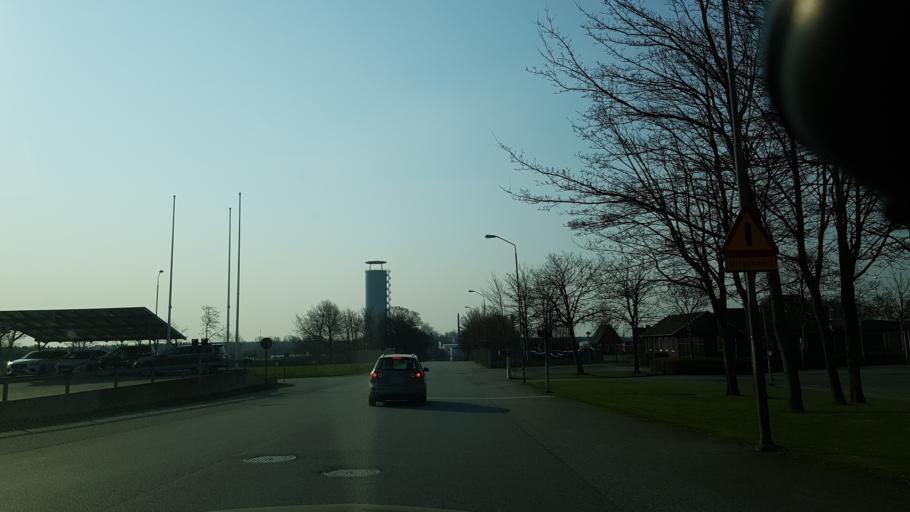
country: SE
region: Skane
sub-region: Ystads Kommun
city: Ystad
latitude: 55.4441
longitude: 13.8395
